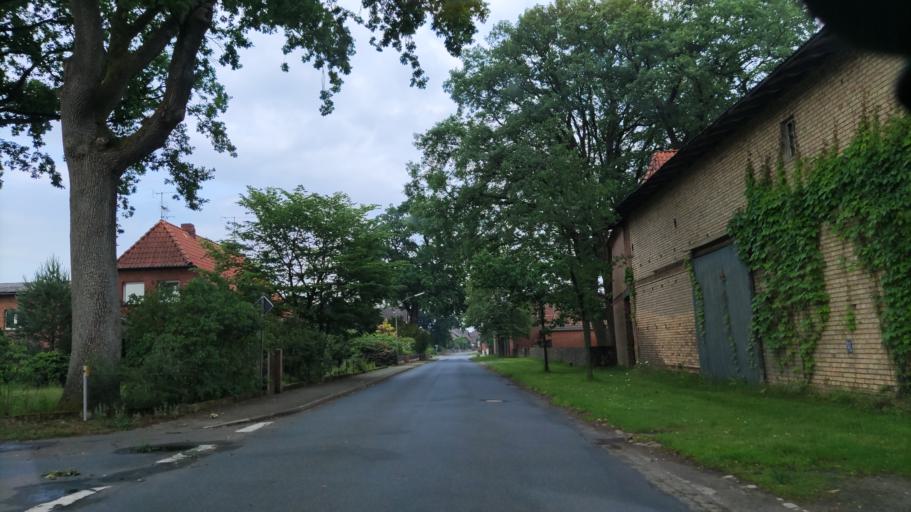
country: DE
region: Lower Saxony
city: Suderburg
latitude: 52.9307
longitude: 10.4411
